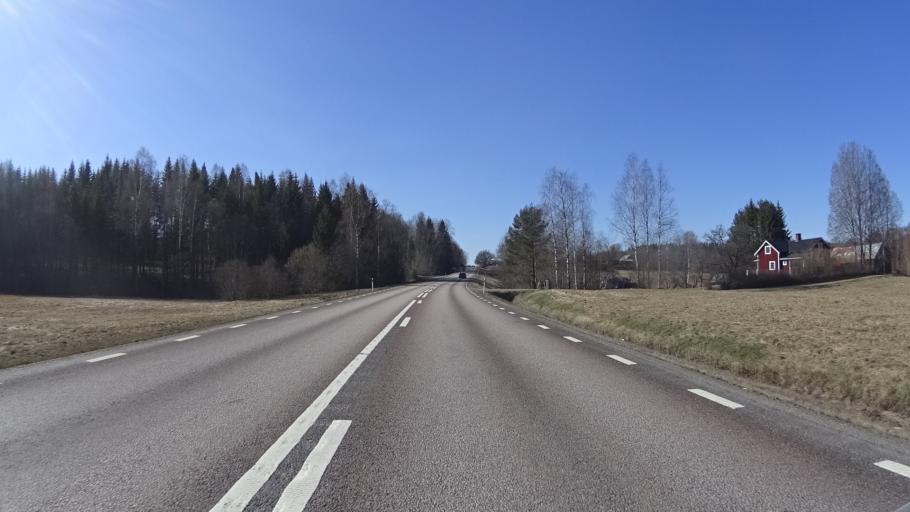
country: SE
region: Vaermland
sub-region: Karlstads Kommun
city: Edsvalla
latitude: 59.5265
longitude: 13.1333
